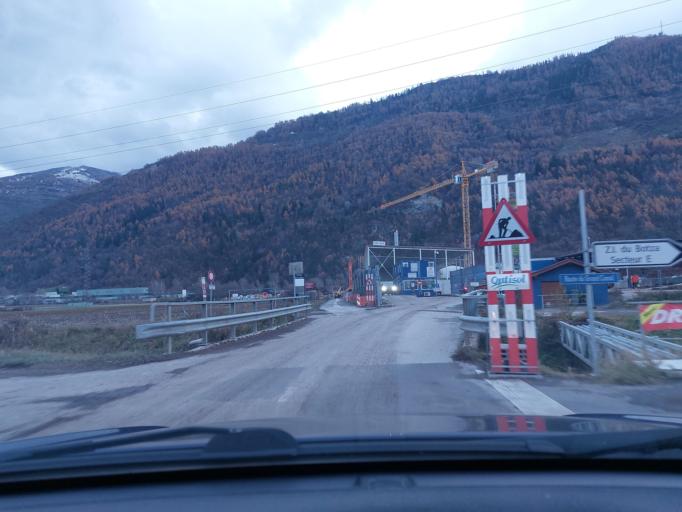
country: CH
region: Valais
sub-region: Conthey District
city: Vetroz
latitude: 46.2039
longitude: 7.2858
